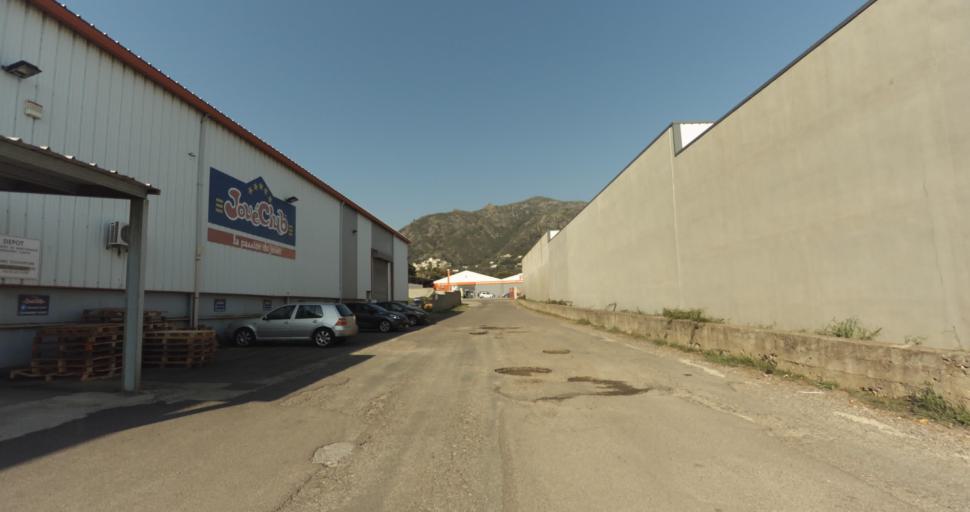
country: FR
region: Corsica
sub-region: Departement de la Haute-Corse
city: Biguglia
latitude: 42.6329
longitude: 9.4360
